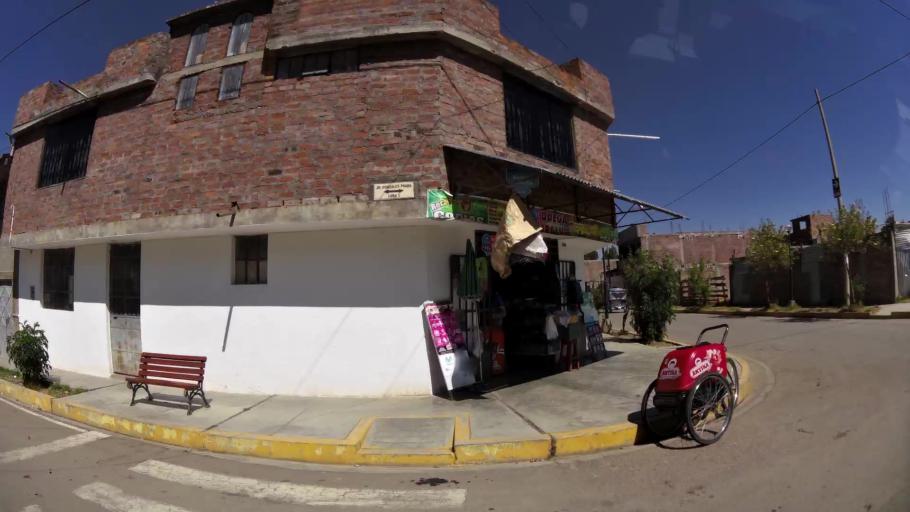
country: PE
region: Junin
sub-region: Provincia de Concepcion
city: Concepcion
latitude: -11.9155
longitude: -75.3176
